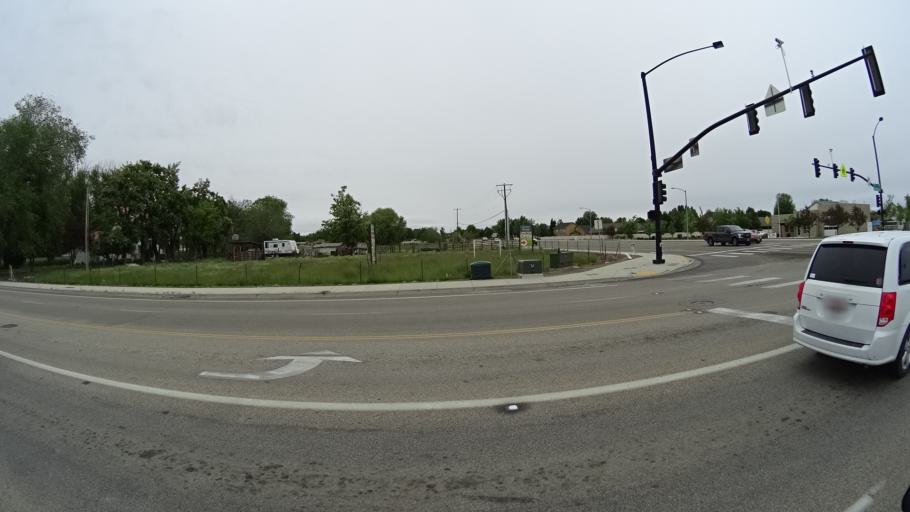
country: US
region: Idaho
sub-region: Ada County
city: Meridian
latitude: 43.6340
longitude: -116.4134
